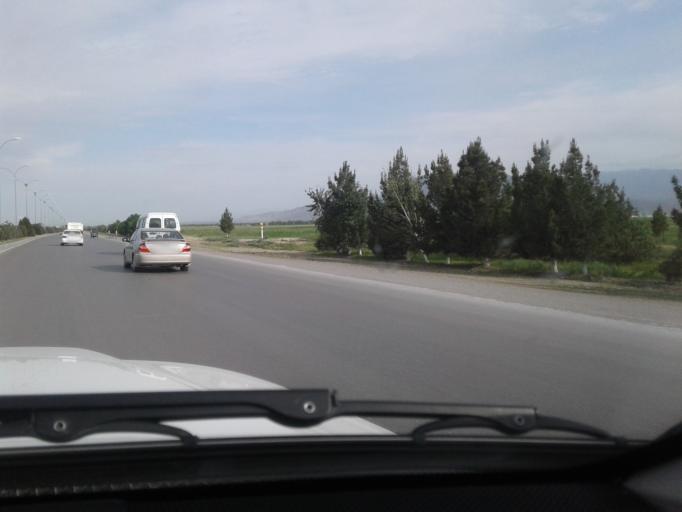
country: TM
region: Ahal
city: Abadan
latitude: 38.1428
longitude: 57.9959
